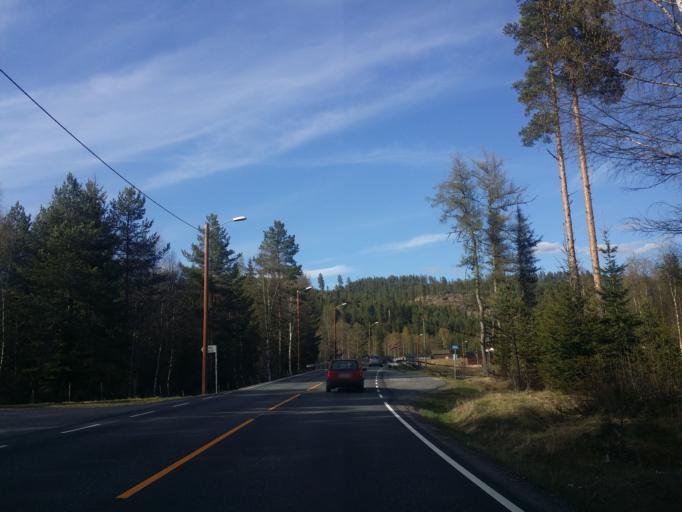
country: NO
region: Buskerud
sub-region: Kongsberg
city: Kongsberg
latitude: 59.6257
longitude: 9.4740
